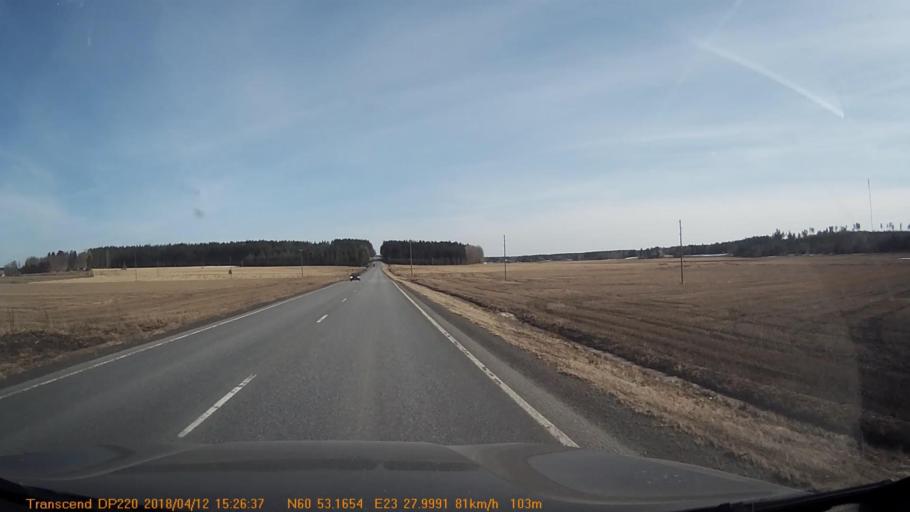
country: FI
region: Haeme
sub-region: Forssa
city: Jokioinen
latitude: 60.8853
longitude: 23.4682
